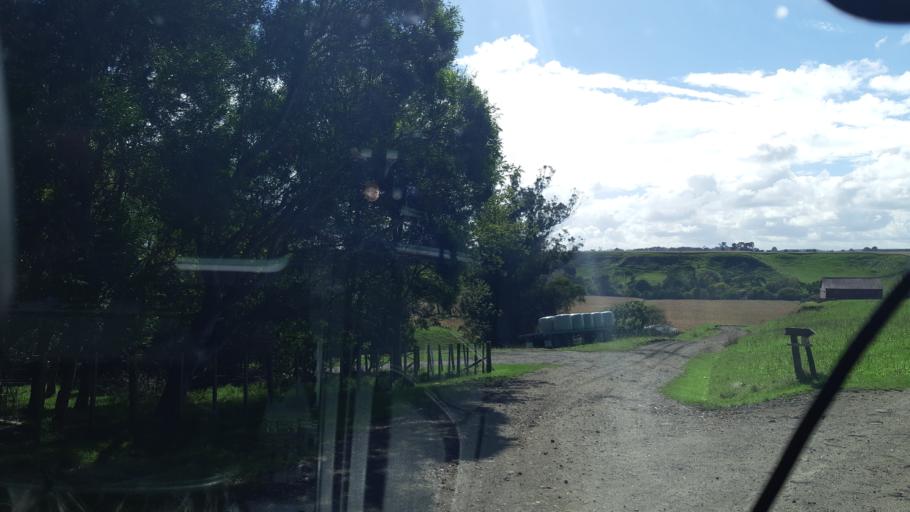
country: NZ
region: Manawatu-Wanganui
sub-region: Wanganui District
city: Wanganui
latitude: -39.9747
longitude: 175.1228
